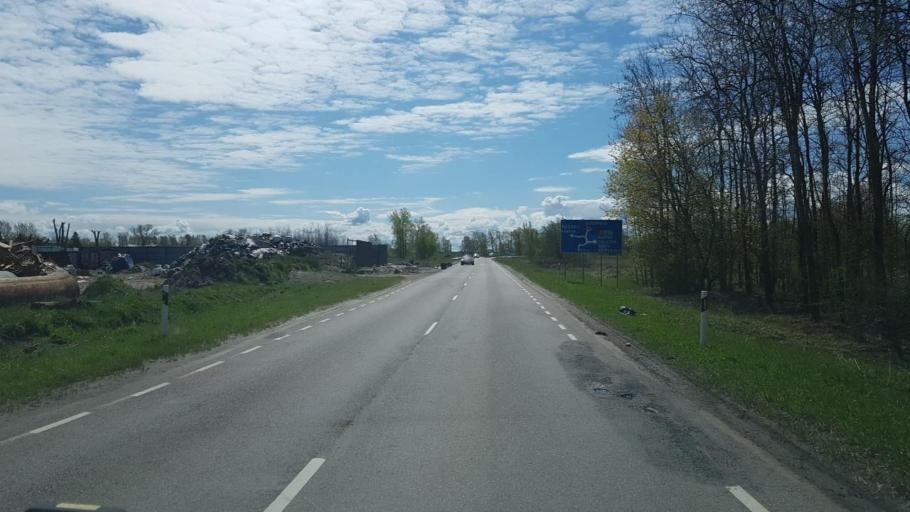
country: EE
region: Harju
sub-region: Maardu linn
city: Maardu
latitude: 59.4598
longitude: 24.9872
